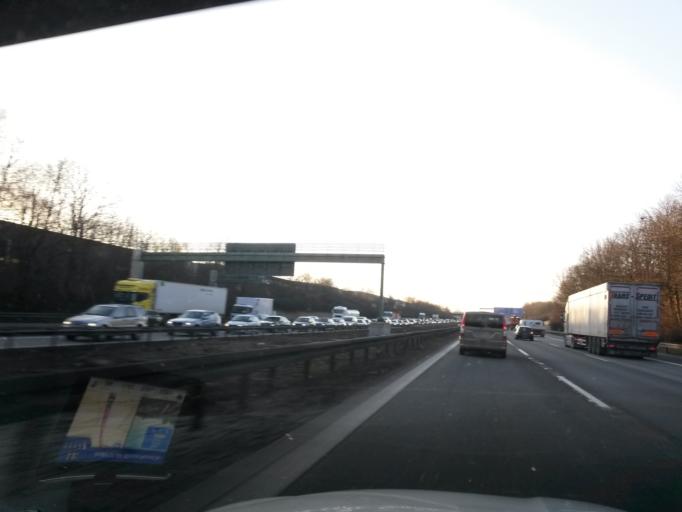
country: DE
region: Bavaria
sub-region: Upper Bavaria
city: Feldkirchen
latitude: 48.1562
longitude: 11.7503
